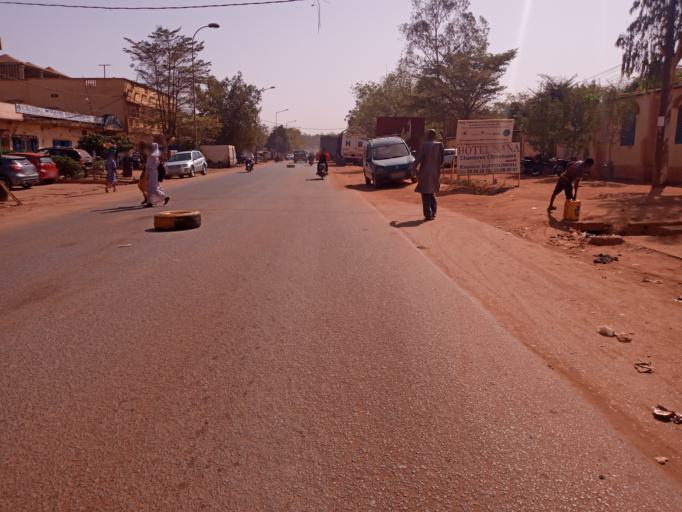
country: ML
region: Bamako
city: Bamako
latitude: 12.6076
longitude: -8.0029
